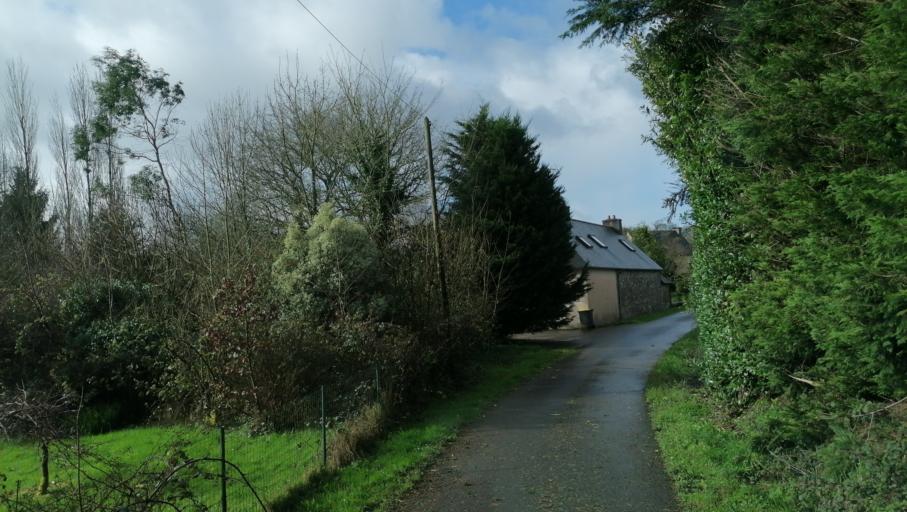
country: FR
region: Brittany
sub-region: Departement des Cotes-d'Armor
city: Lanrodec
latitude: 48.4838
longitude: -3.0377
